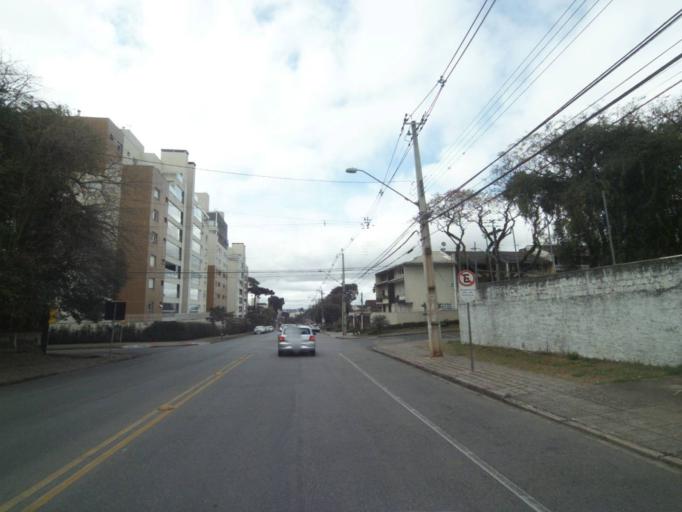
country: BR
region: Parana
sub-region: Curitiba
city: Curitiba
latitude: -25.4594
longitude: -49.2824
